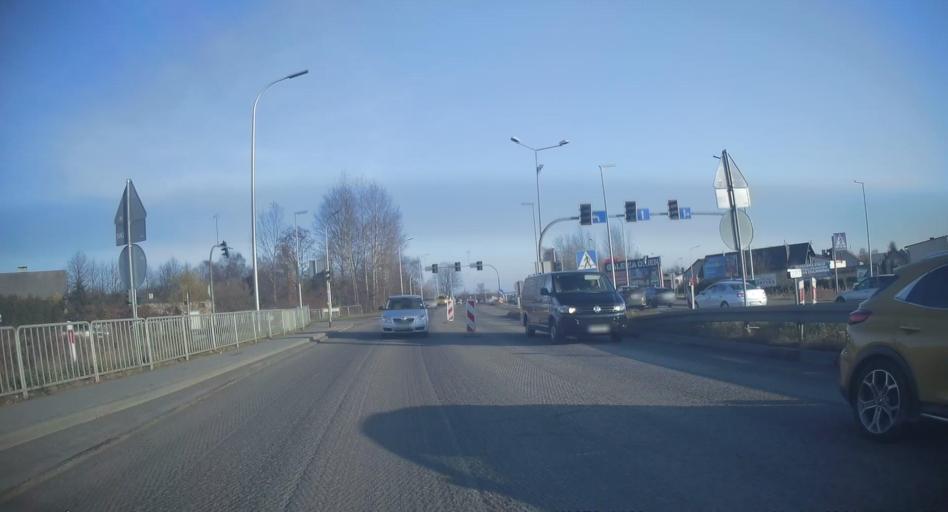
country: PL
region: Lesser Poland Voivodeship
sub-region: Powiat olkuski
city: Boleslaw
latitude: 50.3083
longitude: 19.4693
